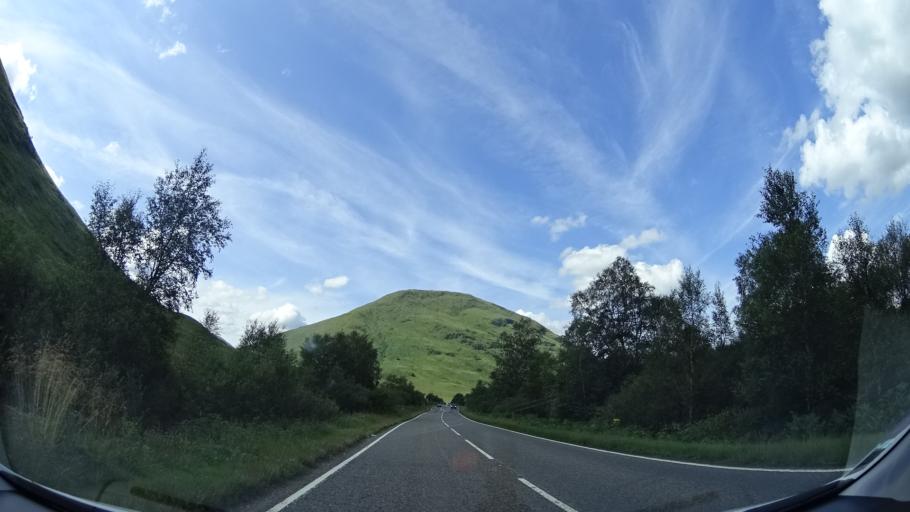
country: GB
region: Scotland
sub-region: Highland
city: Fort William
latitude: 56.6620
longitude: -5.0514
